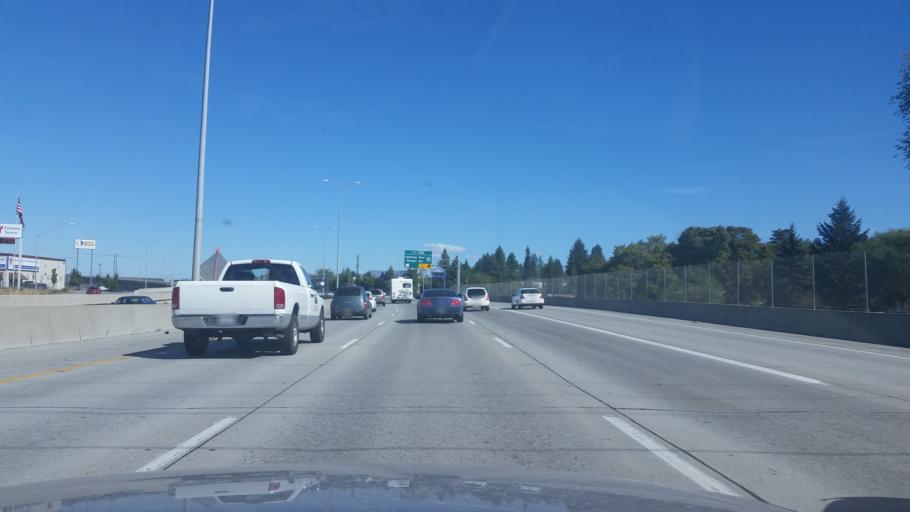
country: US
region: Washington
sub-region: Spokane County
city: Dishman
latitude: 47.6537
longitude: -117.3302
